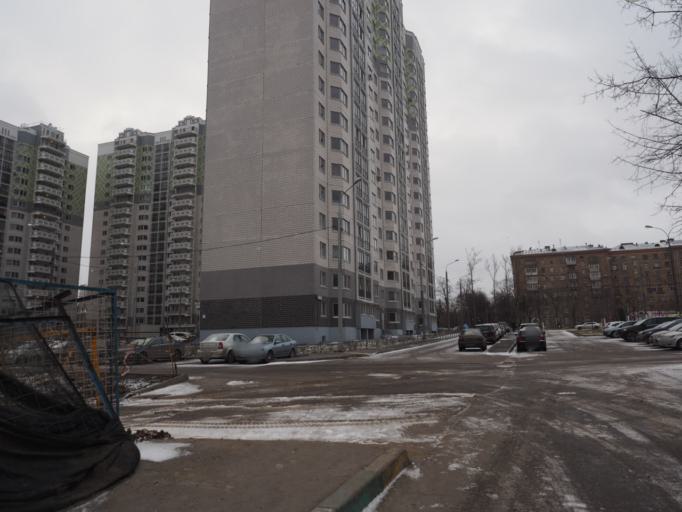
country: RU
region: Moscow
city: Novyye Cheremushki
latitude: 55.6881
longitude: 37.5780
